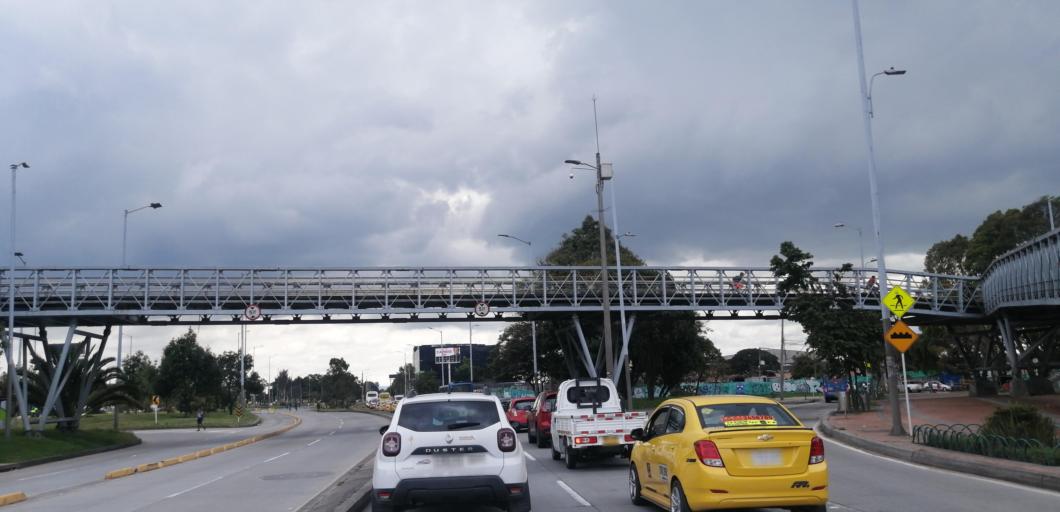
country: CO
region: Bogota D.C.
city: Bogota
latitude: 4.6850
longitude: -74.1227
